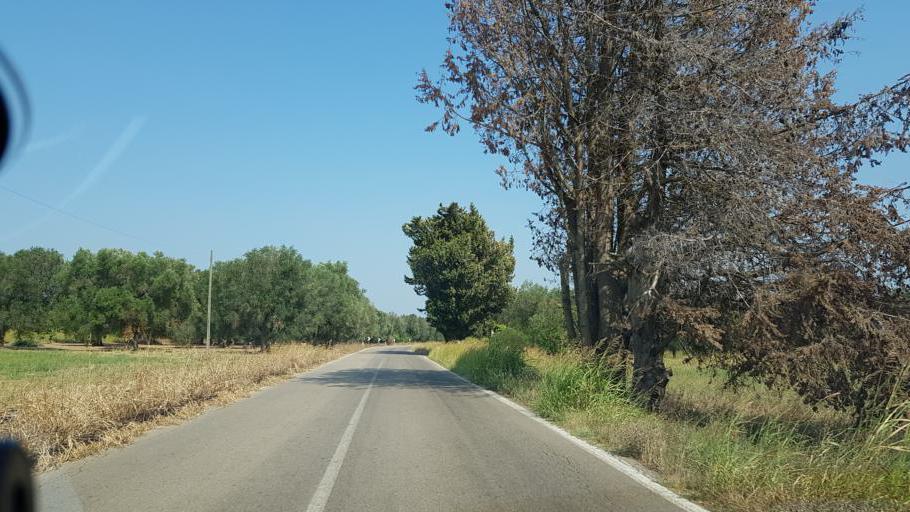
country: IT
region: Apulia
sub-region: Provincia di Brindisi
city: Oria
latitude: 40.4955
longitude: 17.6802
